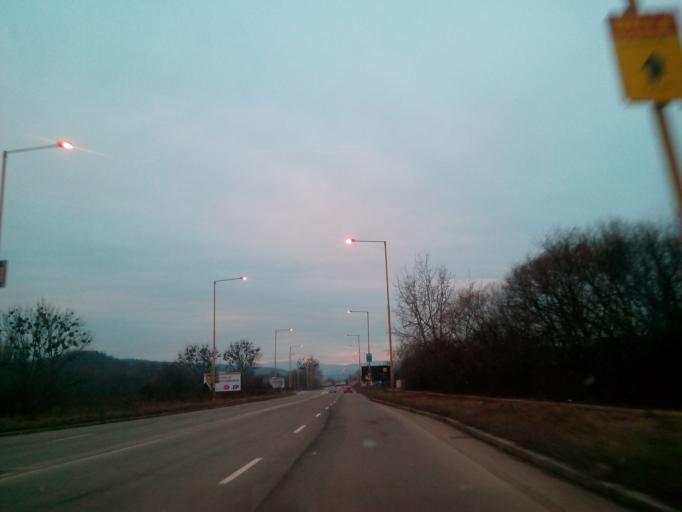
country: SK
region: Kosicky
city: Kosice
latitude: 48.6988
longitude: 21.2256
